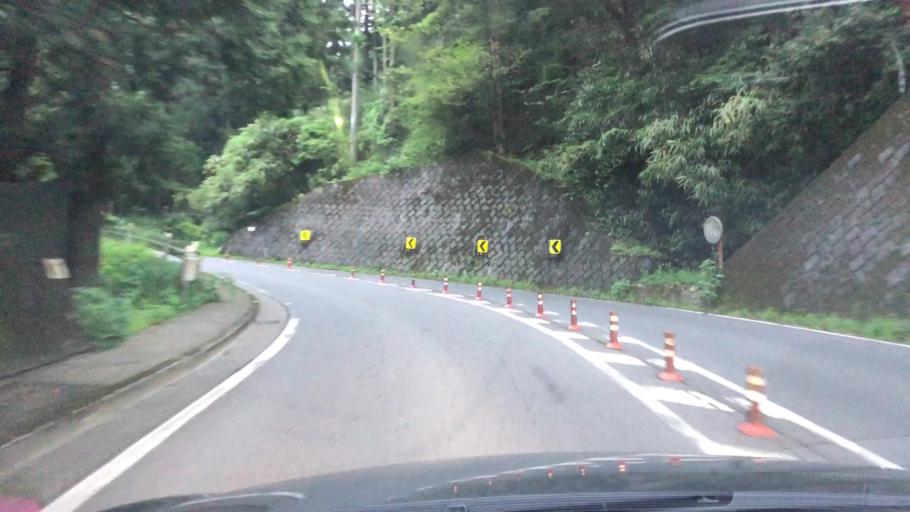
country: JP
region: Tokyo
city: Ome
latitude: 35.7761
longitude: 139.2175
